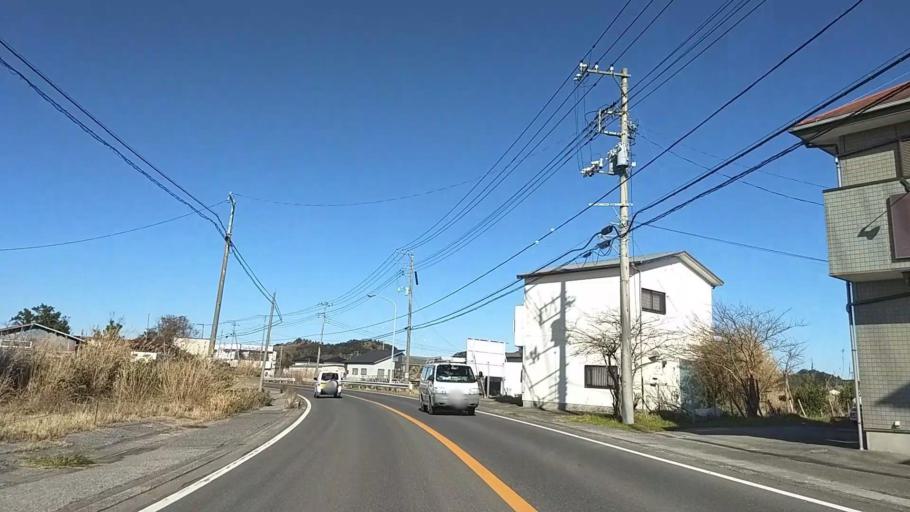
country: JP
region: Chiba
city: Ohara
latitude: 35.3049
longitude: 140.4007
